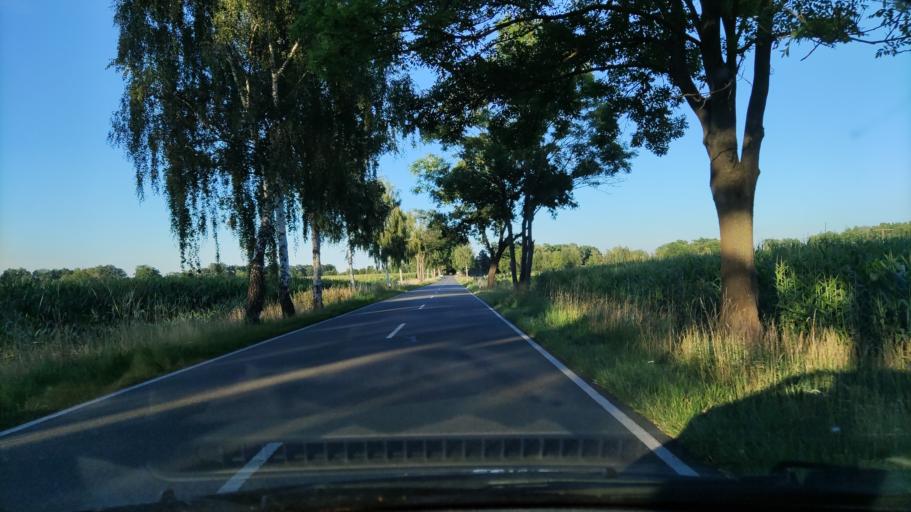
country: DE
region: Lower Saxony
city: Jameln
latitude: 53.0436
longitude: 11.1095
